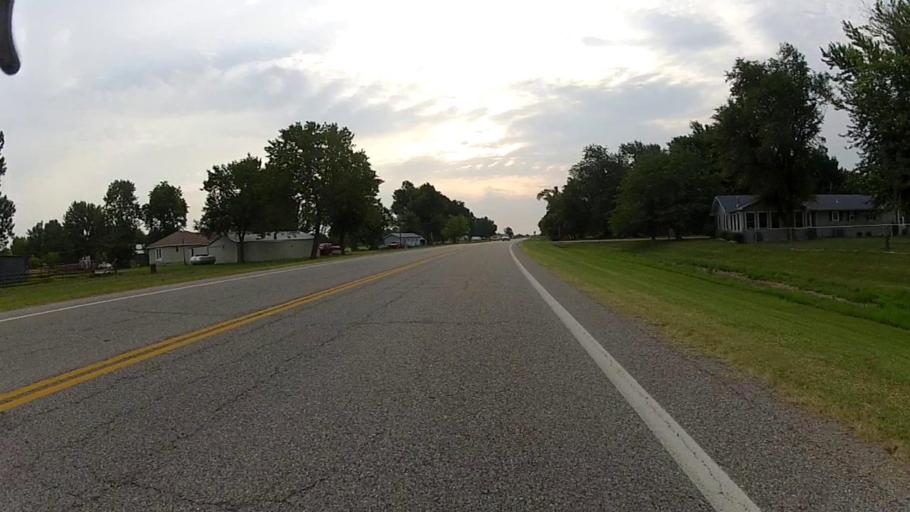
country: US
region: Kansas
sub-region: Labette County
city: Oswego
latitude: 37.1764
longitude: -95.0008
